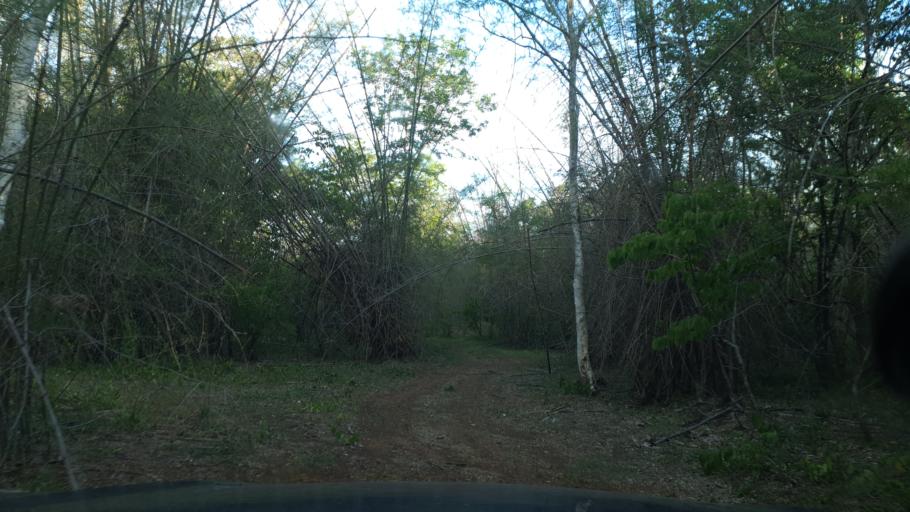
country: TH
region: Lampang
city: Sop Prap
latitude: 17.9657
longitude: 99.3511
